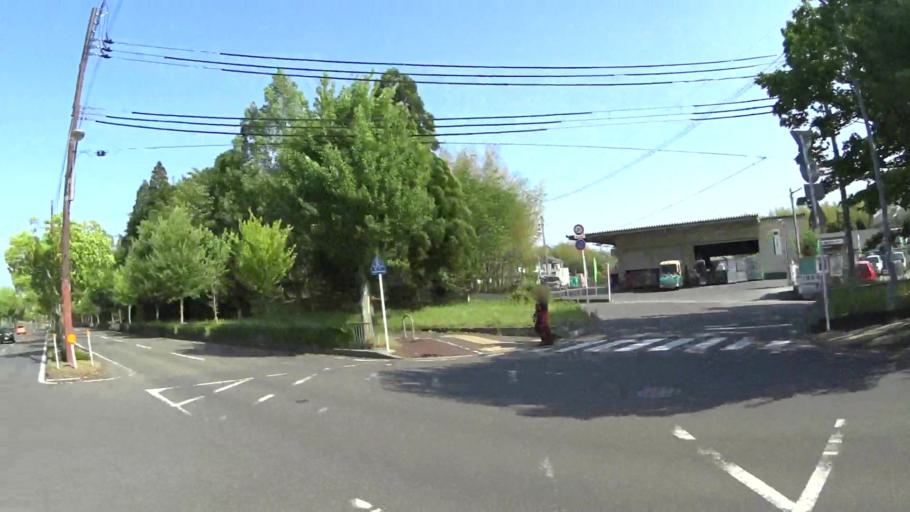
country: JP
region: Kyoto
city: Muko
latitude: 34.9560
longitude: 135.6731
